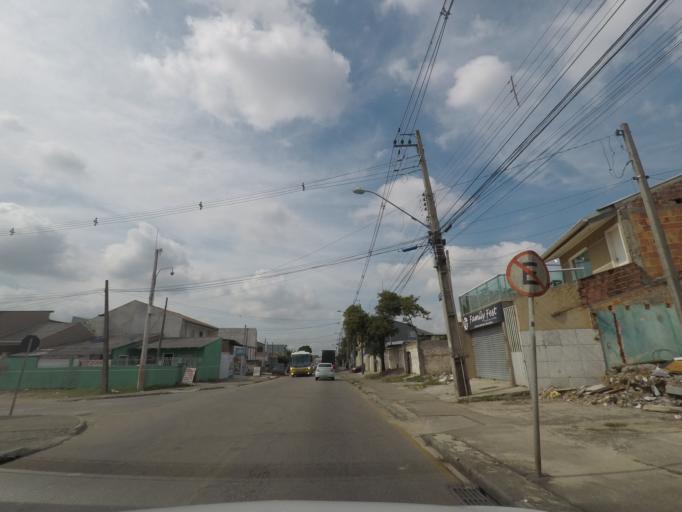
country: BR
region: Parana
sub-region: Pinhais
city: Pinhais
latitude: -25.4656
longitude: -49.1921
